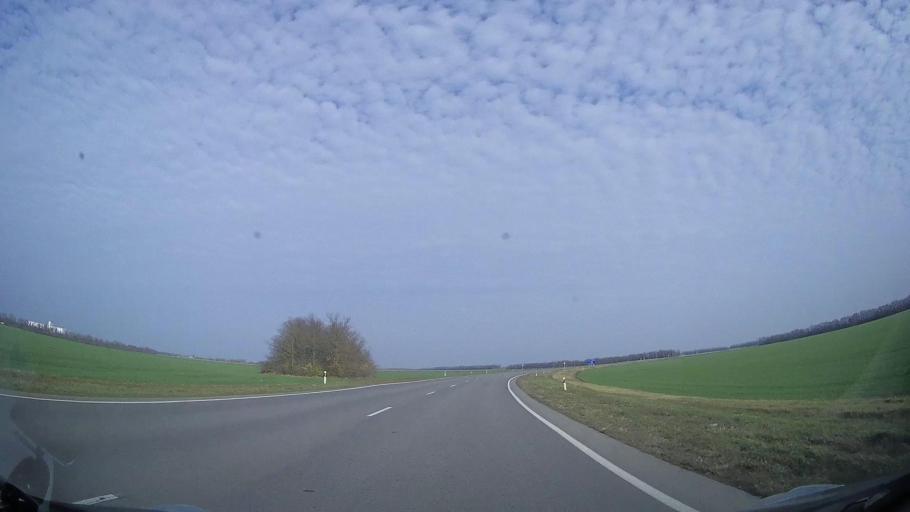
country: RU
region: Rostov
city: Tselina
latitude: 46.5211
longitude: 41.0735
